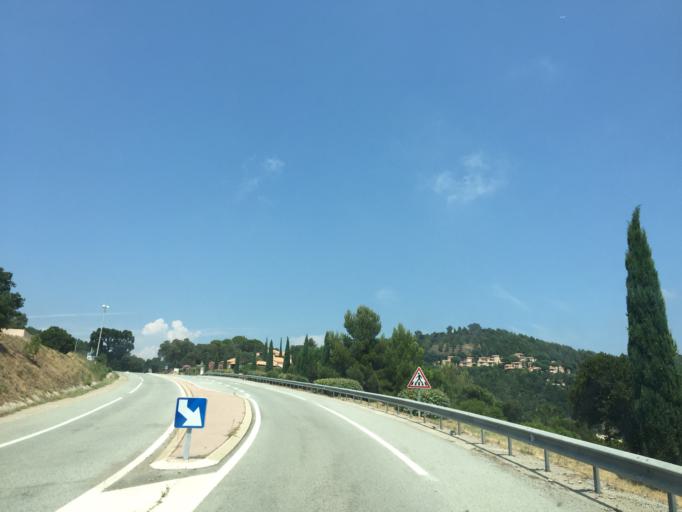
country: FR
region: Provence-Alpes-Cote d'Azur
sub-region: Departement du Var
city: Sainte-Maxime
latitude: 43.3573
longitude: 6.6735
